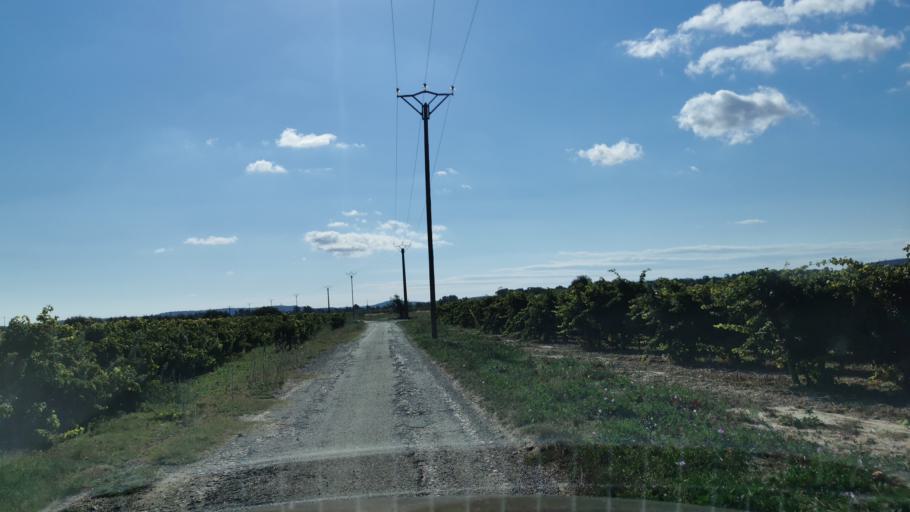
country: FR
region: Languedoc-Roussillon
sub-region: Departement de l'Aude
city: Canet
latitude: 43.2433
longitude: 2.8633
